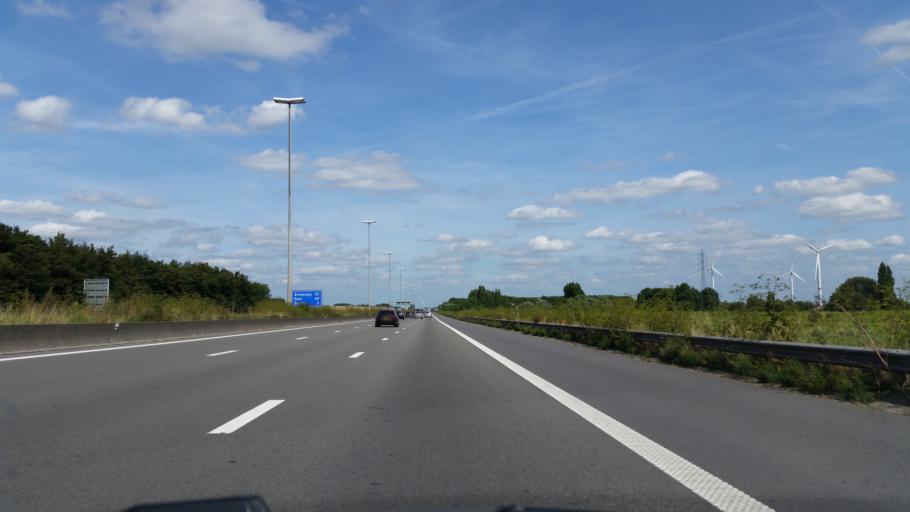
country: BE
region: Flanders
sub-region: Provincie West-Vlaanderen
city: Harelbeke
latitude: 50.8231
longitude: 3.3092
